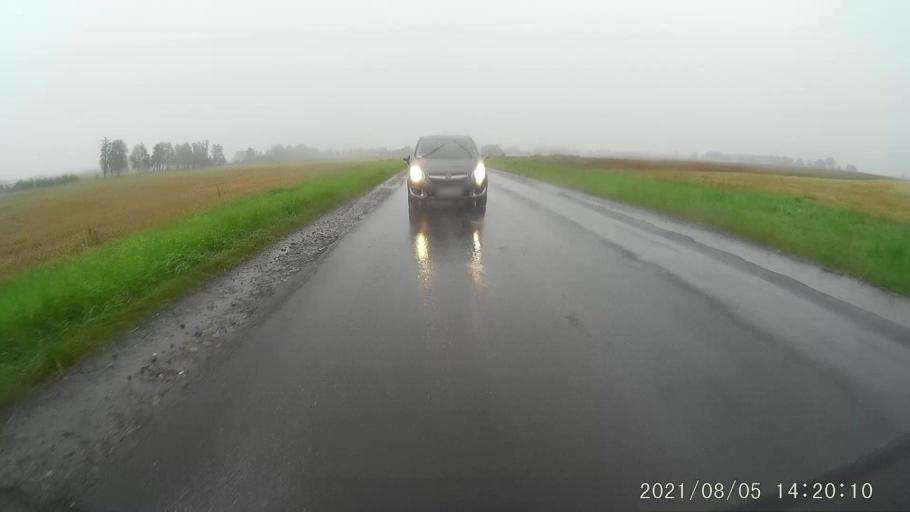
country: PL
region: Opole Voivodeship
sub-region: Powiat nyski
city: Korfantow
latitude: 50.4688
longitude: 17.6824
